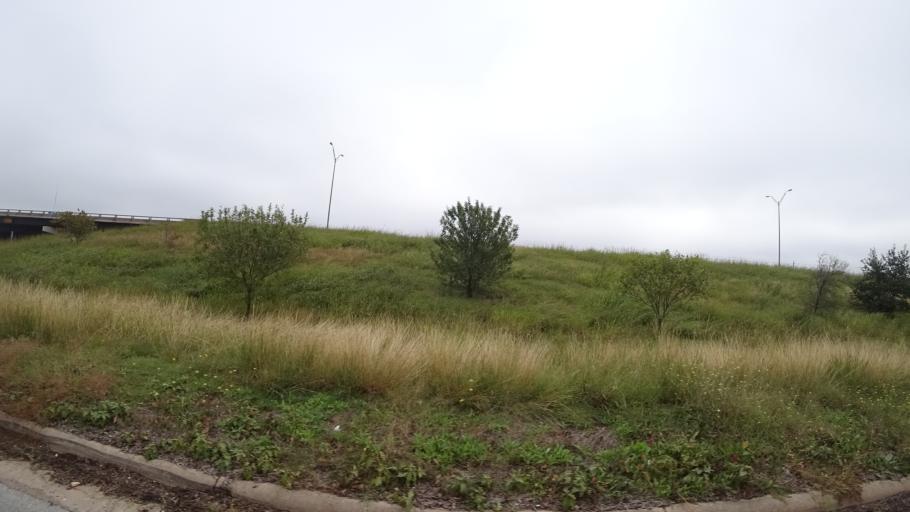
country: US
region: Texas
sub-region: Travis County
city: Shady Hollow
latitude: 30.2200
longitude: -97.8374
